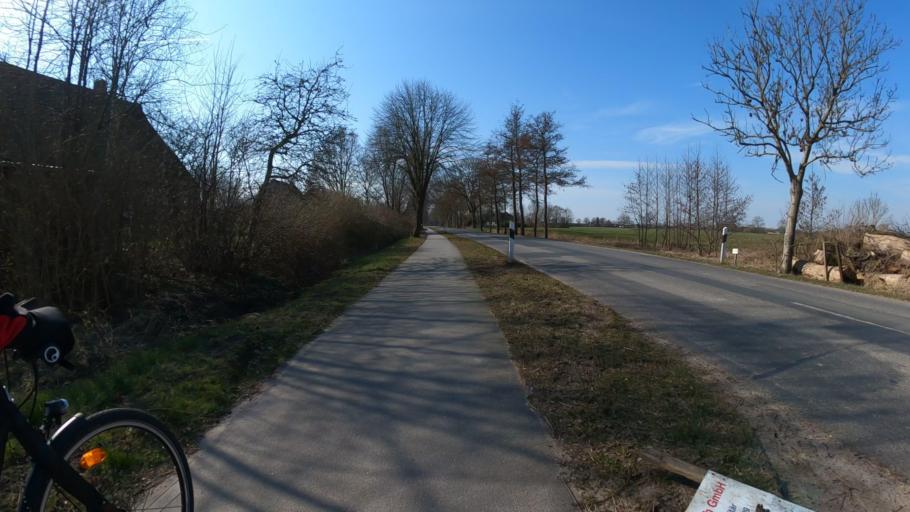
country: DE
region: Schleswig-Holstein
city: Neuendeich
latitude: 53.6751
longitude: 9.5923
